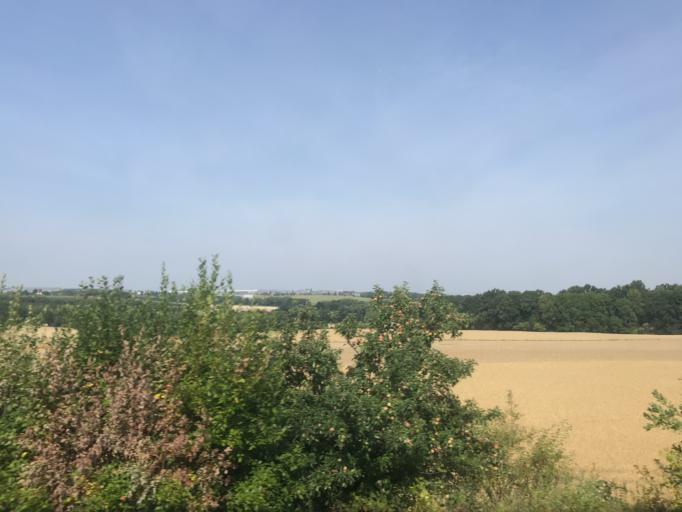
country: CZ
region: Central Bohemia
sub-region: Okres Praha-Vychod
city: Ricany
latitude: 49.9663
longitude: 14.6539
